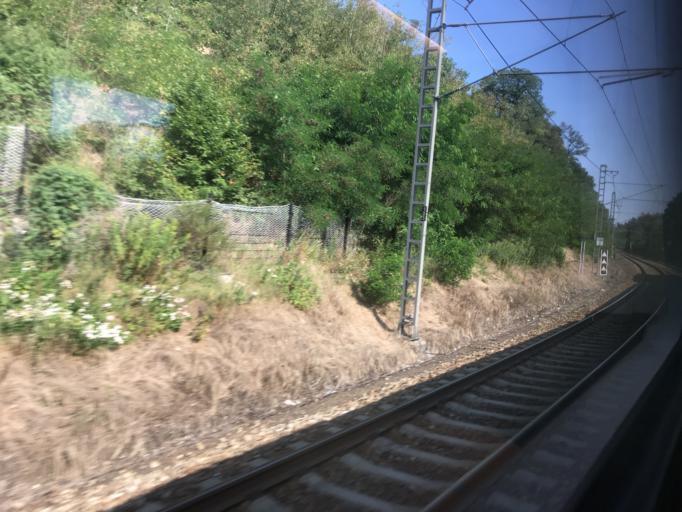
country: CZ
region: Central Bohemia
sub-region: Okres Benesov
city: Cercany
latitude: 49.8782
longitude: 14.7266
